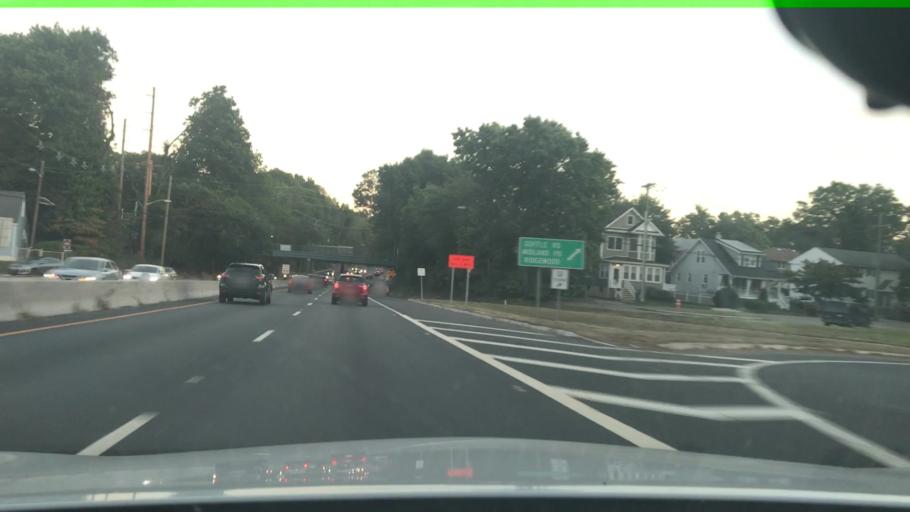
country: US
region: New Jersey
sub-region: Passaic County
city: Hawthorne
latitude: 40.9670
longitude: -74.1534
